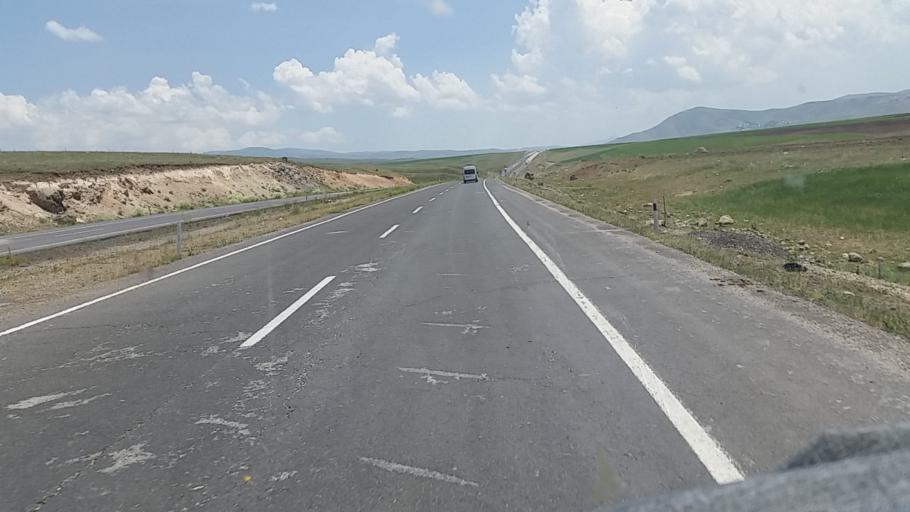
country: TR
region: Agri
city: Taslicay
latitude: 39.6328
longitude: 43.4120
